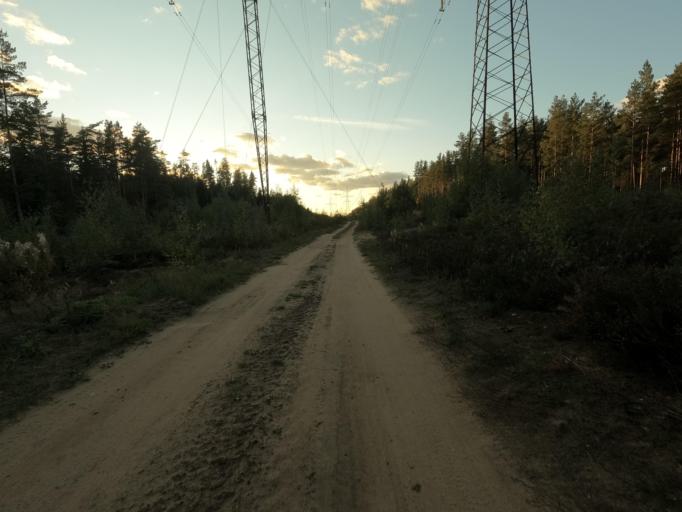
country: RU
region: Leningrad
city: Otradnoye
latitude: 59.8211
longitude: 30.8290
